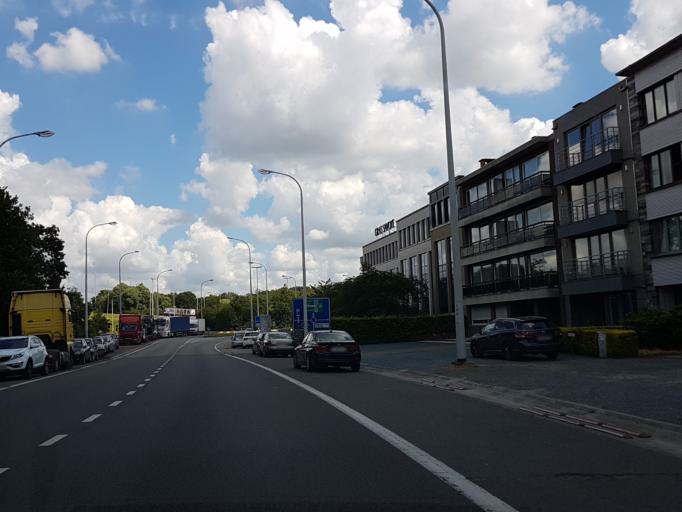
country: BE
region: Flanders
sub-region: Provincie Vlaams-Brabant
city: Wemmel
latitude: 50.8799
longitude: 4.2846
